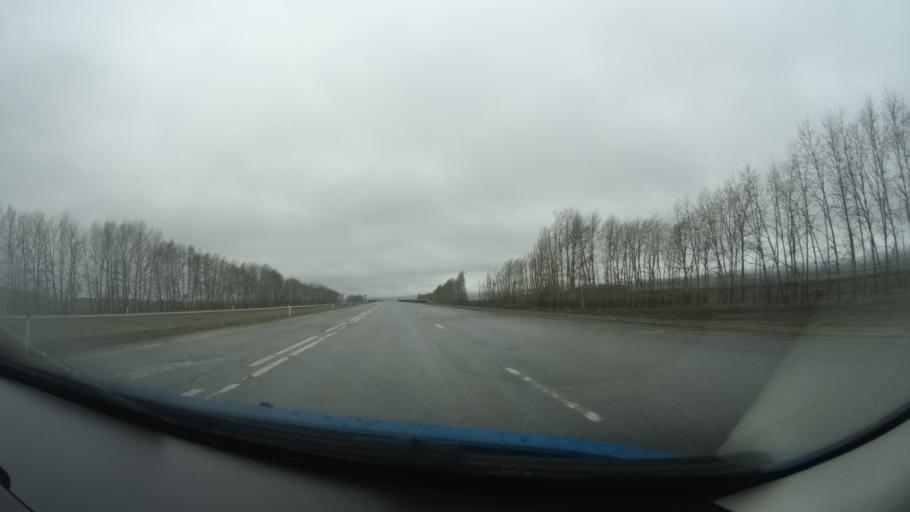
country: RU
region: Bashkortostan
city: Alekseyevka
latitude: 54.7316
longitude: 55.0432
